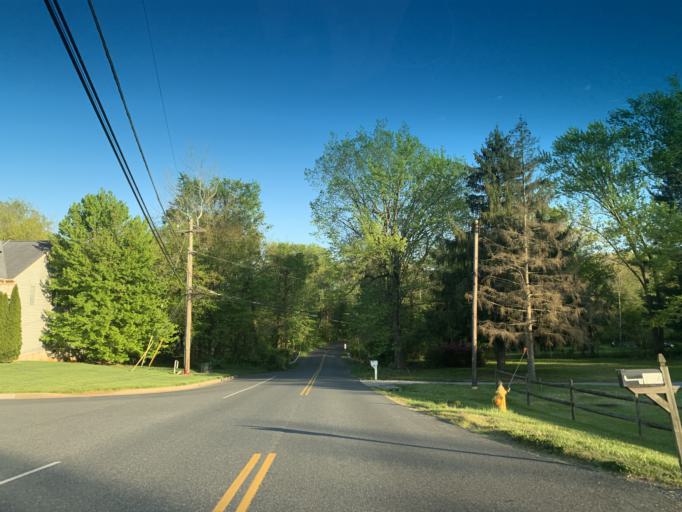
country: US
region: Maryland
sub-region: Harford County
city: Aberdeen
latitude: 39.5328
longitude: -76.1753
